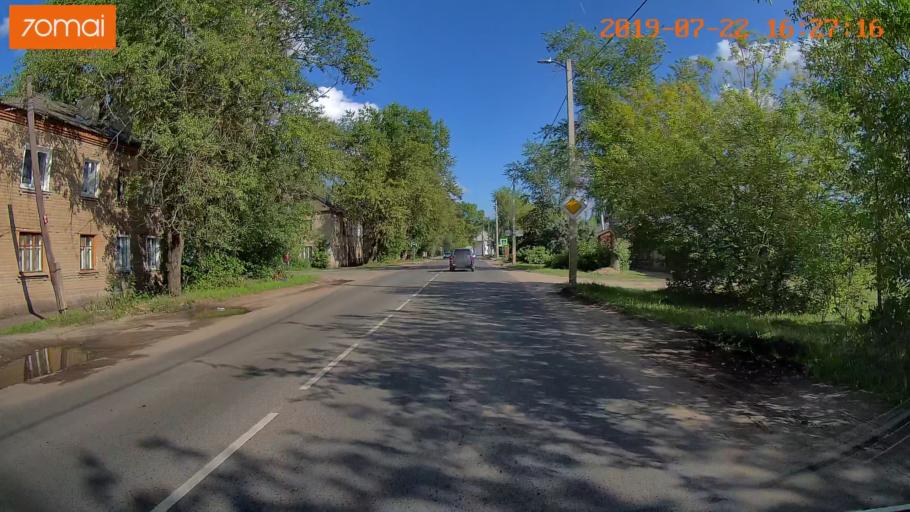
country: RU
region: Ivanovo
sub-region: Gorod Ivanovo
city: Ivanovo
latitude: 57.0448
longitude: 40.9440
